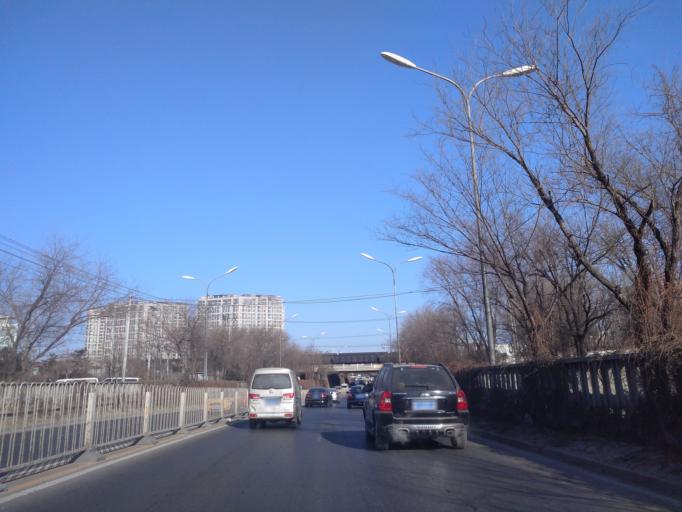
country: CN
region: Beijing
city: Jiugong
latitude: 39.8301
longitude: 116.4701
